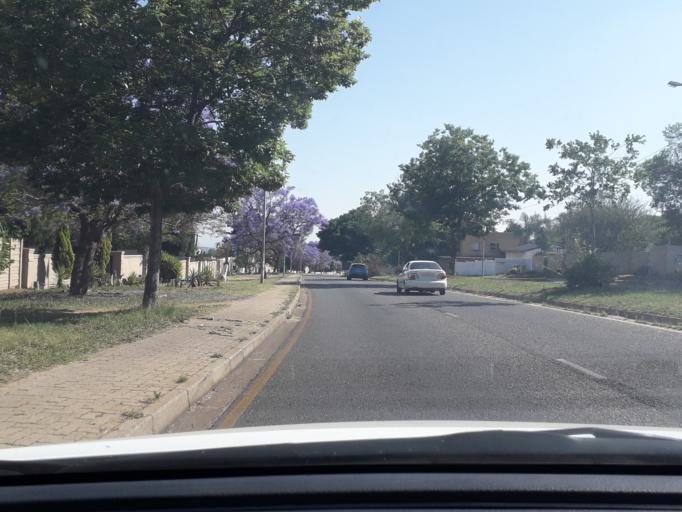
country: ZA
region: Gauteng
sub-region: City of Johannesburg Metropolitan Municipality
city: Roodepoort
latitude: -26.1137
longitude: 27.9724
